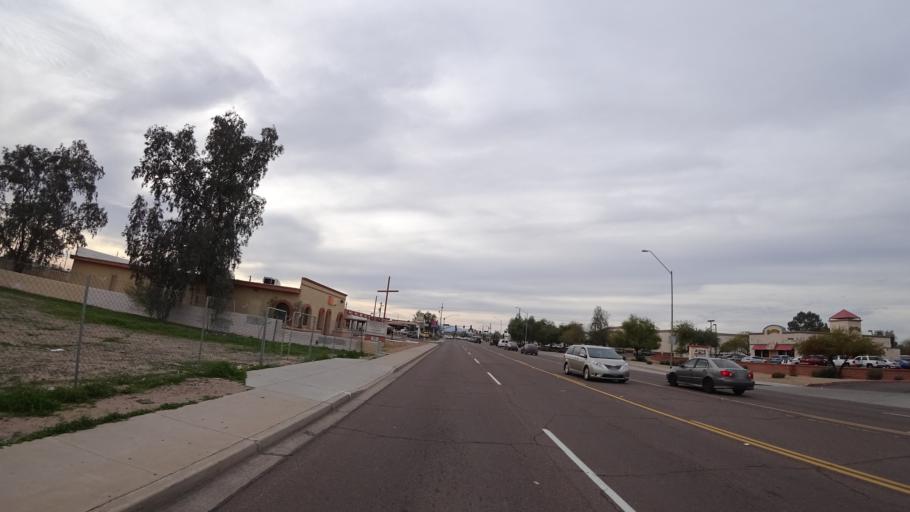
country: US
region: Arizona
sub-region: Maricopa County
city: Peoria
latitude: 33.5808
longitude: -112.2533
